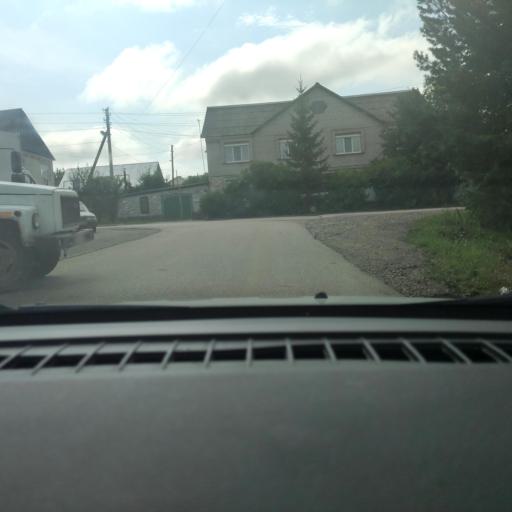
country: RU
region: Perm
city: Lobanovo
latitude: 57.8612
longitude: 56.2808
